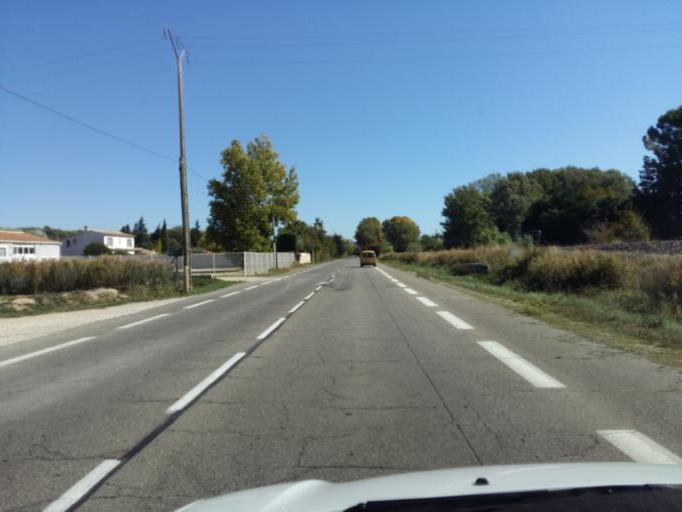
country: FR
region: Provence-Alpes-Cote d'Azur
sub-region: Departement du Vaucluse
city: Lauris
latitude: 43.7481
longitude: 5.2898
